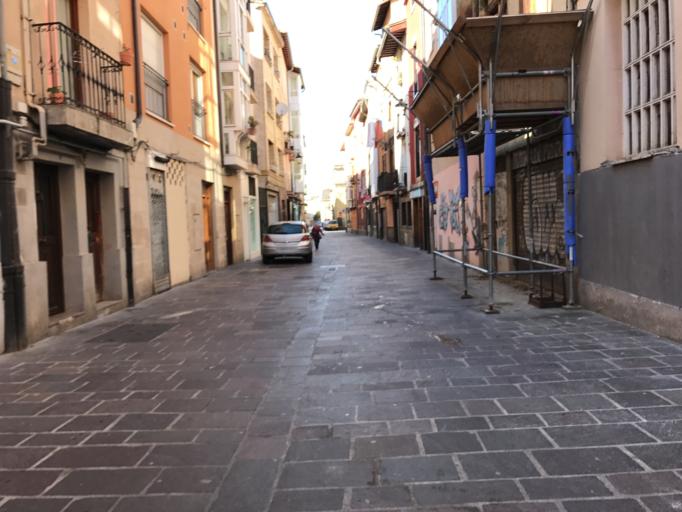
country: ES
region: Basque Country
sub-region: Provincia de Alava
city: Gasteiz / Vitoria
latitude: 42.8482
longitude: -2.6696
